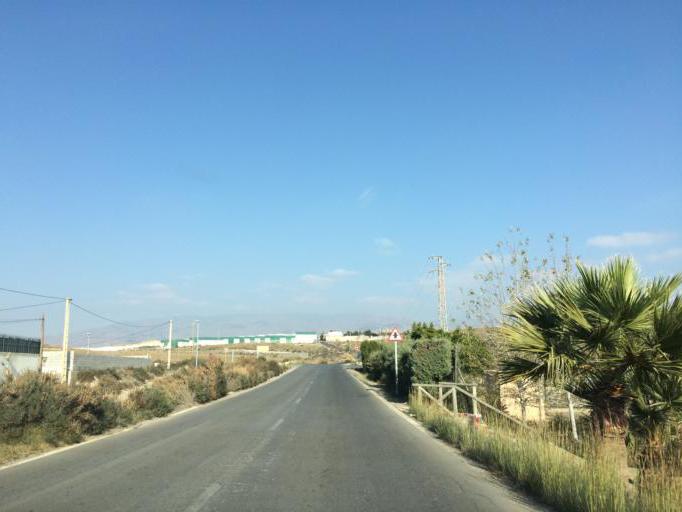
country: ES
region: Andalusia
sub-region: Provincia de Almeria
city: Viator
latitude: 36.8690
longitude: -2.4188
